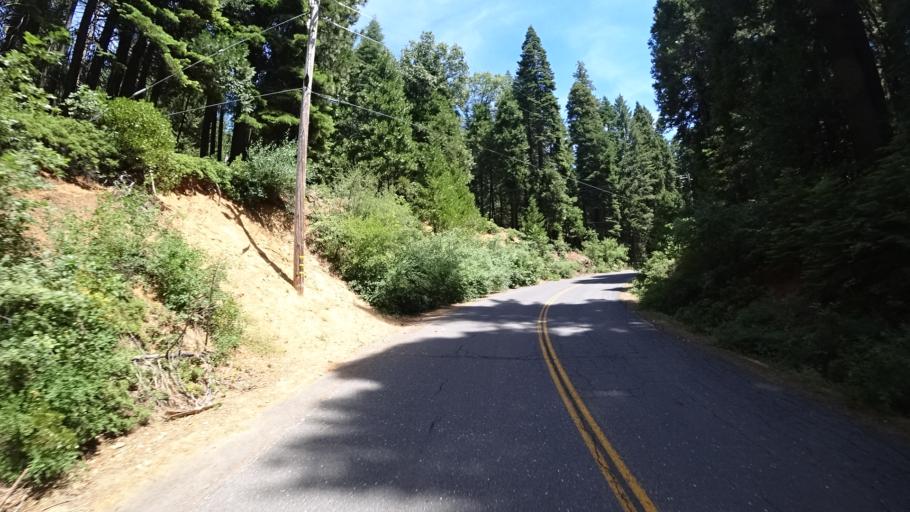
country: US
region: California
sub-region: Calaveras County
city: Arnold
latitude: 38.3080
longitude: -120.2668
